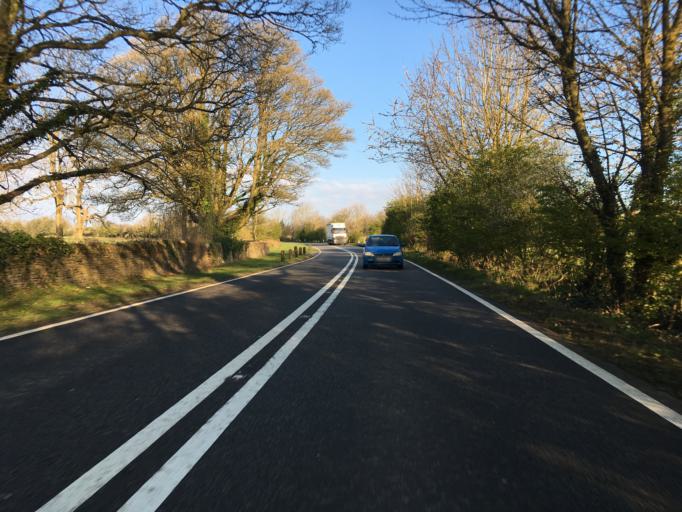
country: GB
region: England
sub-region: Gloucestershire
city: Shipton Village
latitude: 51.8675
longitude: -1.9820
